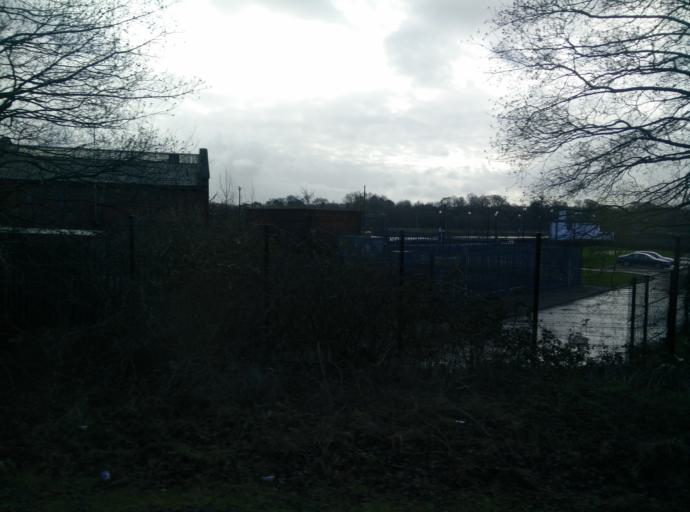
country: GB
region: Northern Ireland
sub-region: City of Belfast
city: Belfast
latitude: 54.5903
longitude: -5.9218
